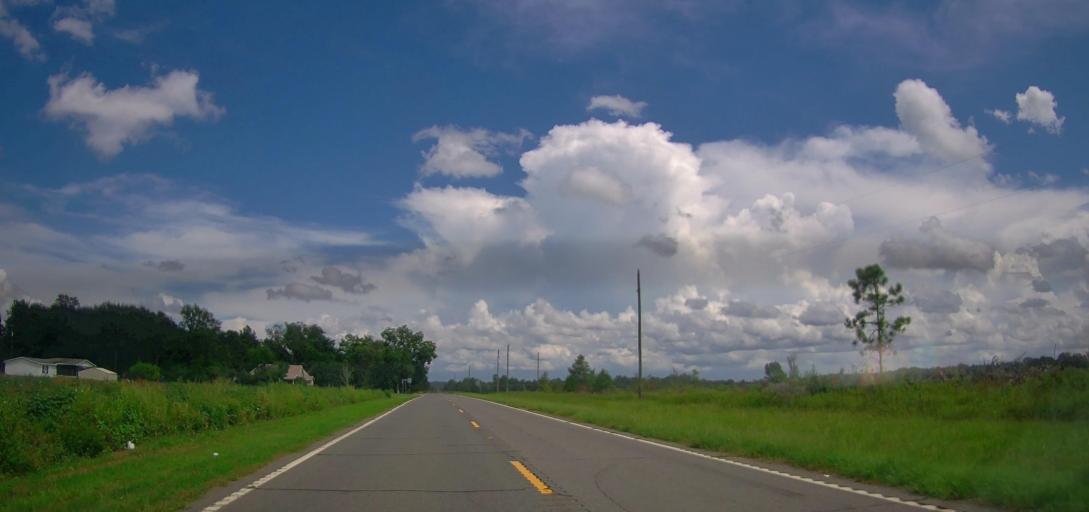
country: US
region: Georgia
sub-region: Macon County
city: Marshallville
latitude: 32.4335
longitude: -84.0669
